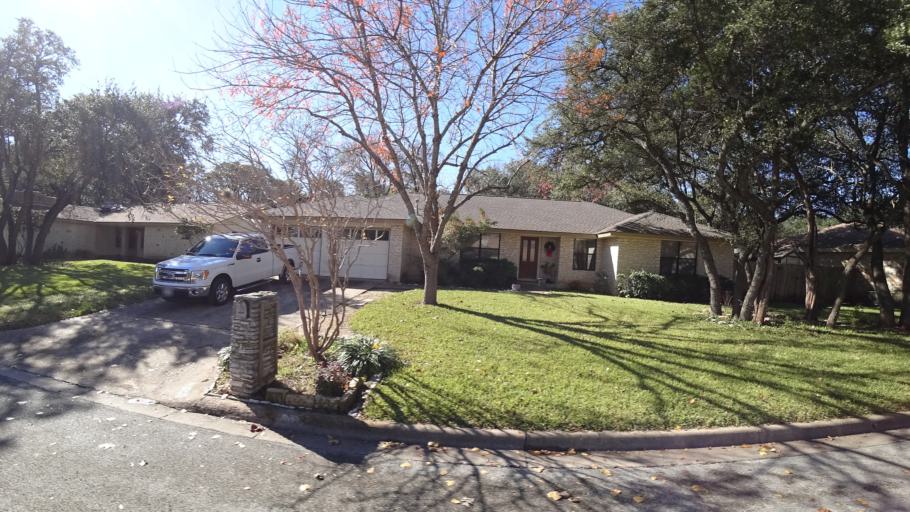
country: US
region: Texas
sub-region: Travis County
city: Wells Branch
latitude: 30.4272
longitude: -97.7134
